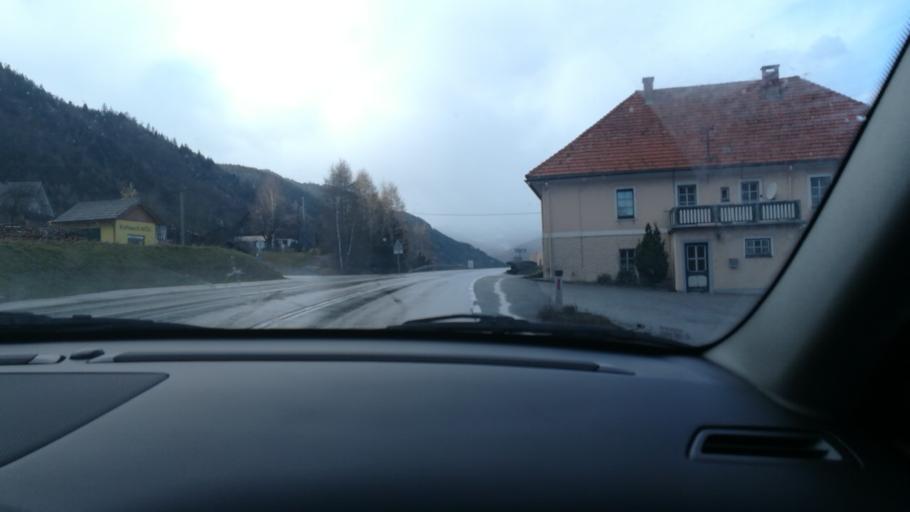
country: AT
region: Styria
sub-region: Politischer Bezirk Murtal
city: Sankt Georgen ob Judenburg
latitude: 47.2010
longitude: 14.5311
